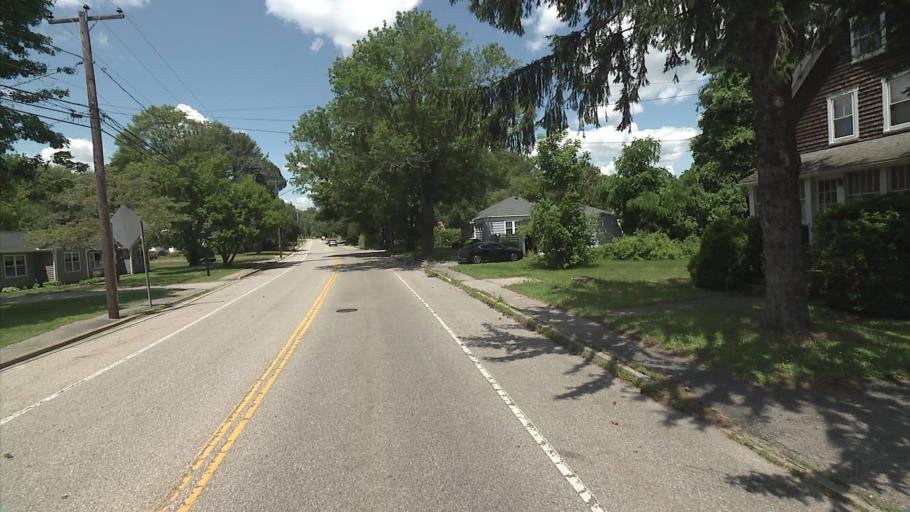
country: US
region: Connecticut
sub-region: New London County
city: Mystic
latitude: 41.3550
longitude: -71.9778
